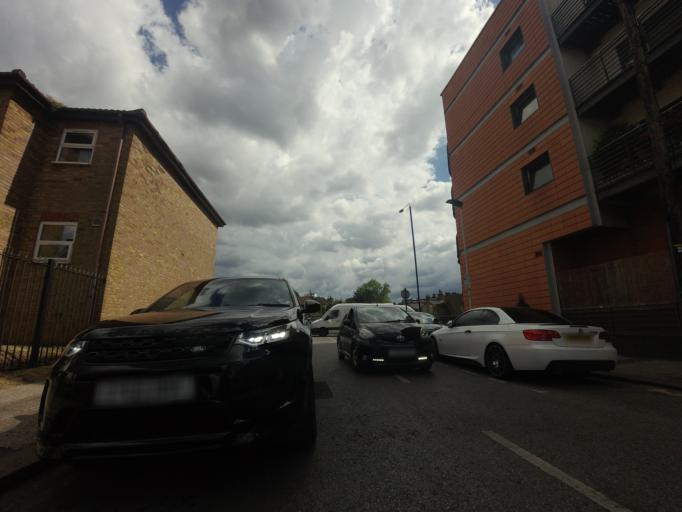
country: GB
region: England
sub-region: Greater London
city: Poplar
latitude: 51.5468
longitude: 0.0076
